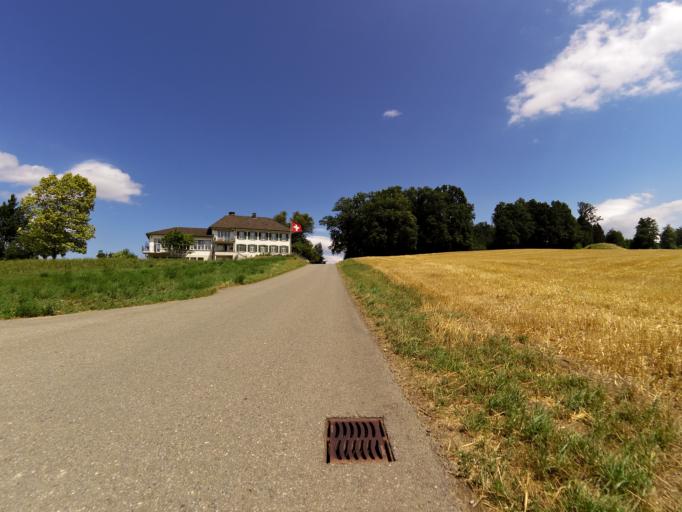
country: CH
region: Thurgau
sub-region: Weinfelden District
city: Maerstetten-Dorf
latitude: 47.6012
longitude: 9.0553
